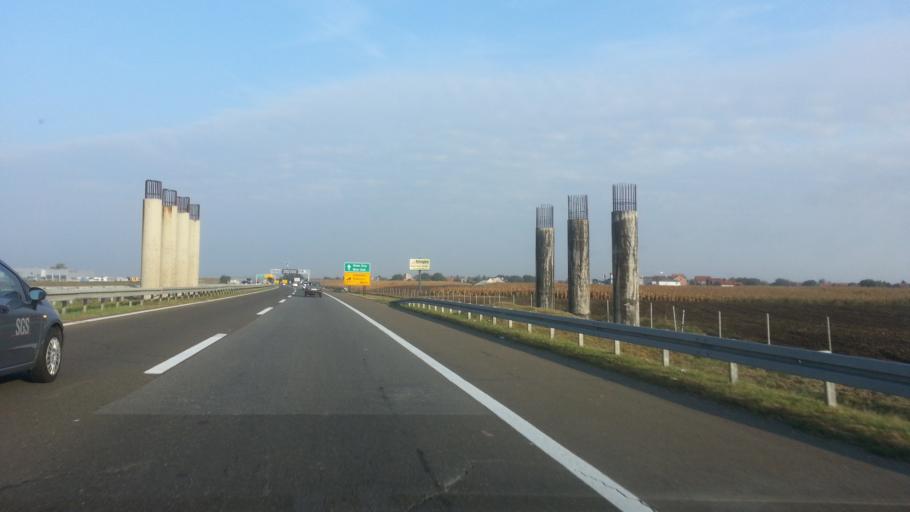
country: RS
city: Novi Banovci
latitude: 44.9383
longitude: 20.2904
